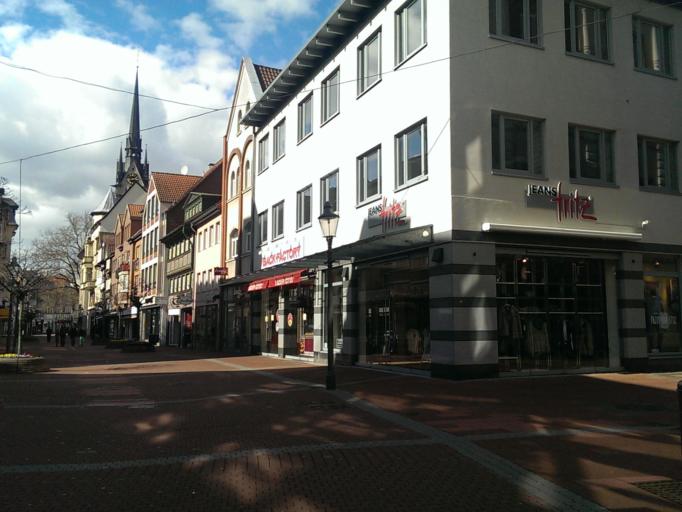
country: DE
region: Lower Saxony
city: Peine
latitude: 52.3213
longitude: 10.2290
